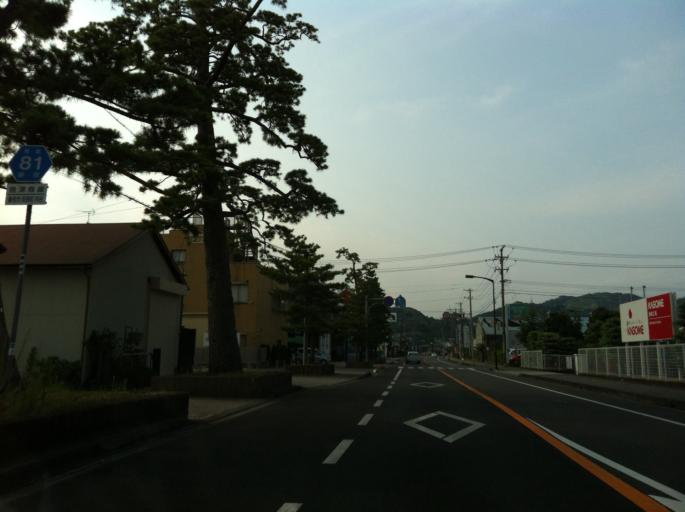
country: JP
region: Shizuoka
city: Fujieda
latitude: 34.9062
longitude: 138.2825
